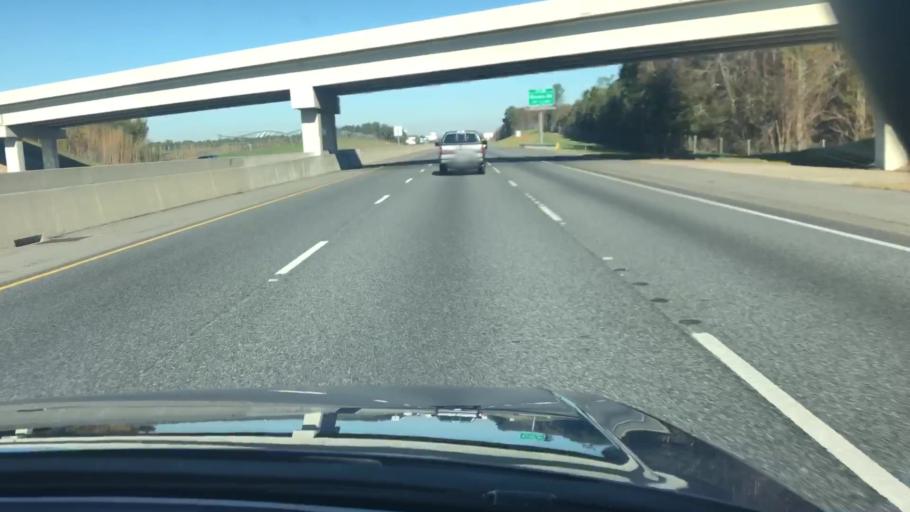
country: US
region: Georgia
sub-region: Turner County
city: Ashburn
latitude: 31.6720
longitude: -83.6124
